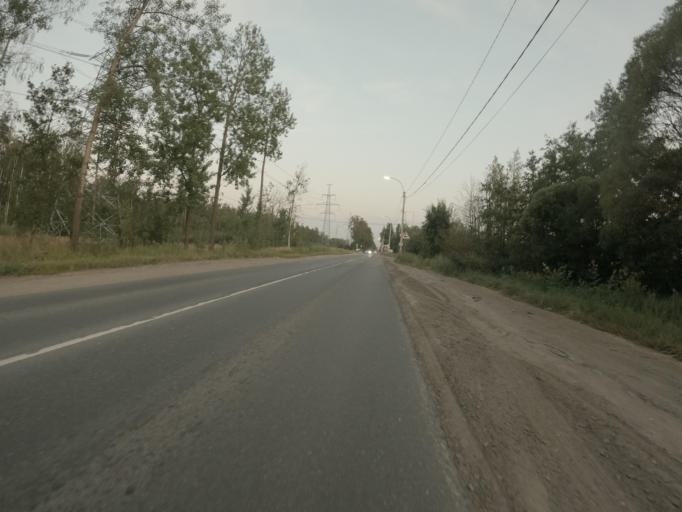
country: RU
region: St.-Petersburg
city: Krasnogvargeisky
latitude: 59.9443
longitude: 30.5208
